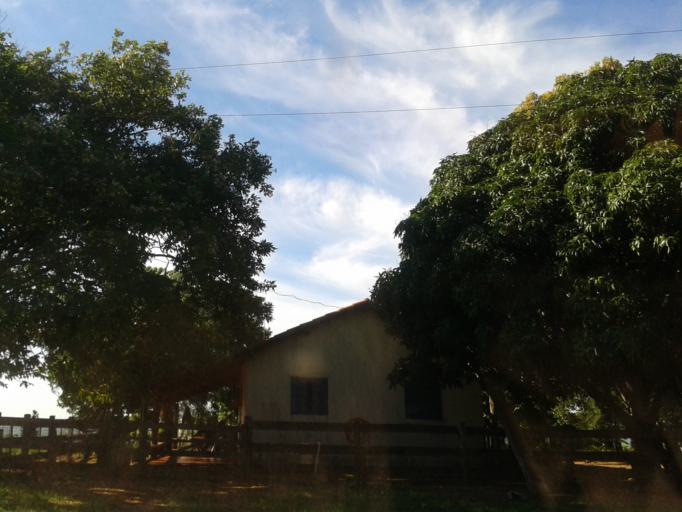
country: BR
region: Minas Gerais
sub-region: Santa Vitoria
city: Santa Vitoria
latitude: -19.1251
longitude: -50.0134
